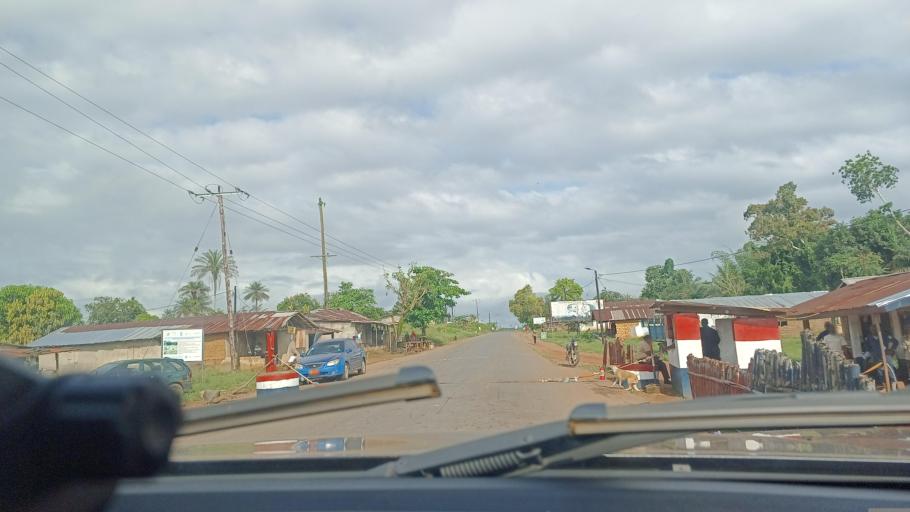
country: LR
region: Bomi
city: Tubmanburg
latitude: 6.7213
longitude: -10.9802
